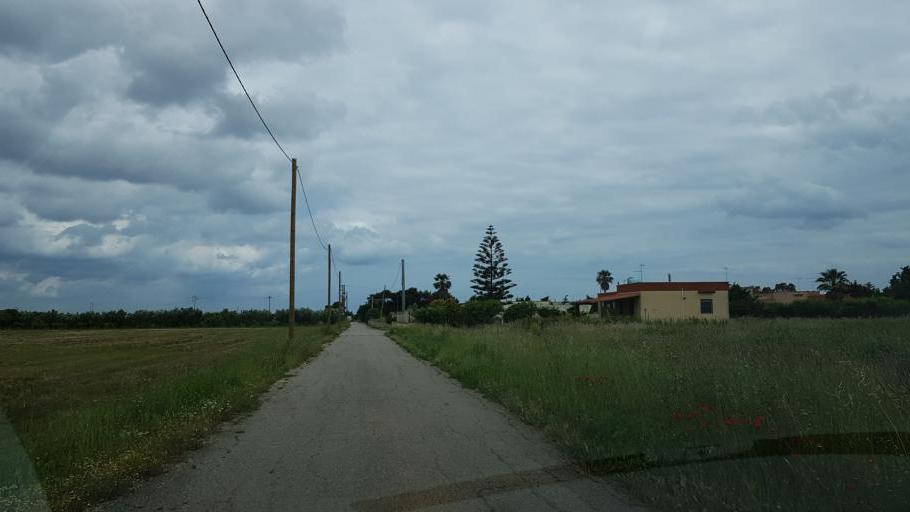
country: IT
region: Apulia
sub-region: Provincia di Brindisi
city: Brindisi
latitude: 40.6342
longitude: 17.8766
